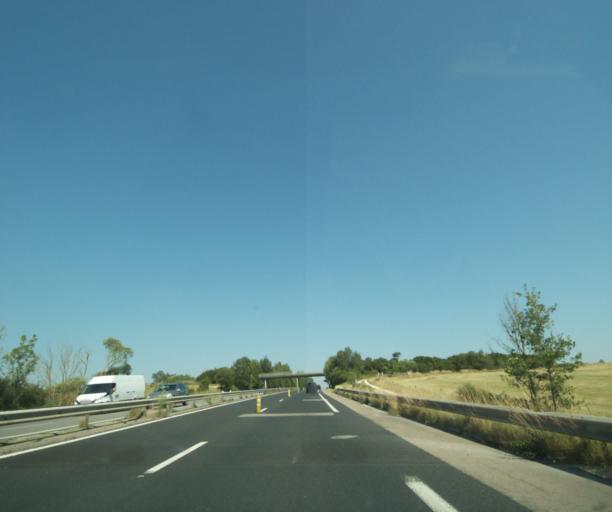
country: FR
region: Lorraine
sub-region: Departement de Meurthe-et-Moselle
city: Domgermain
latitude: 48.6553
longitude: 5.8434
